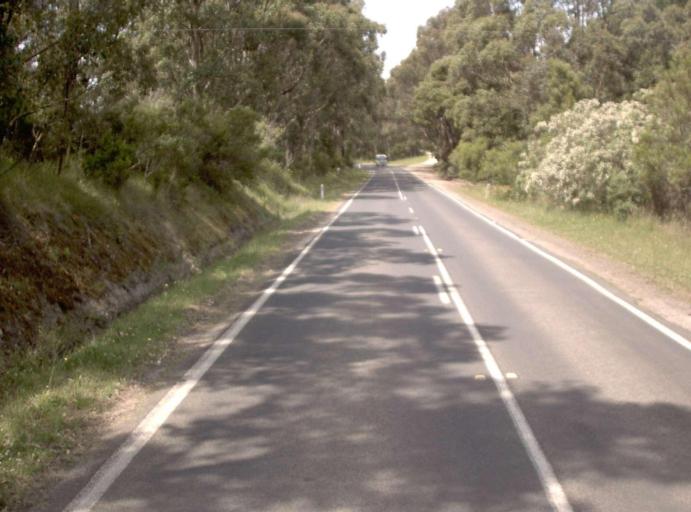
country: AU
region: Victoria
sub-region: Latrobe
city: Traralgon
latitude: -38.3473
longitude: 146.7169
